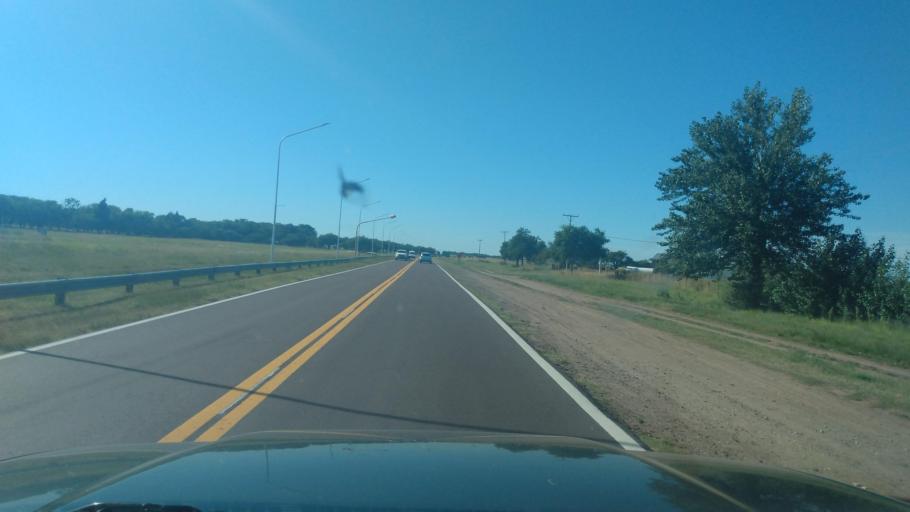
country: AR
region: La Pampa
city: Doblas
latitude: -37.0369
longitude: -64.2879
